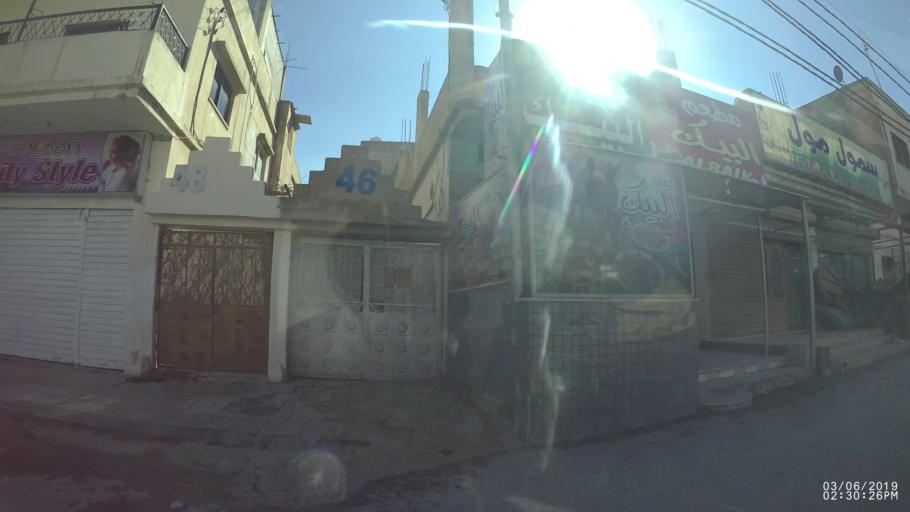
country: JO
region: Zarqa
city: Russeifa
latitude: 32.0326
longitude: 36.0381
